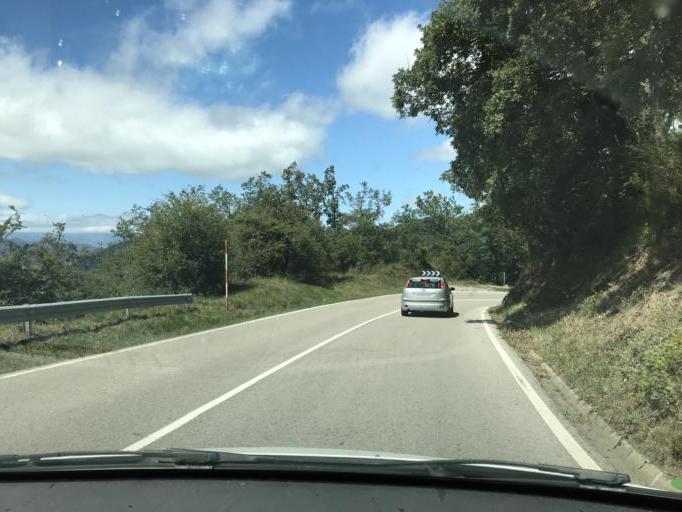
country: ES
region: Cantabria
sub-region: Provincia de Cantabria
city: Cabezon de Liebana
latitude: 43.0649
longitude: -4.4815
